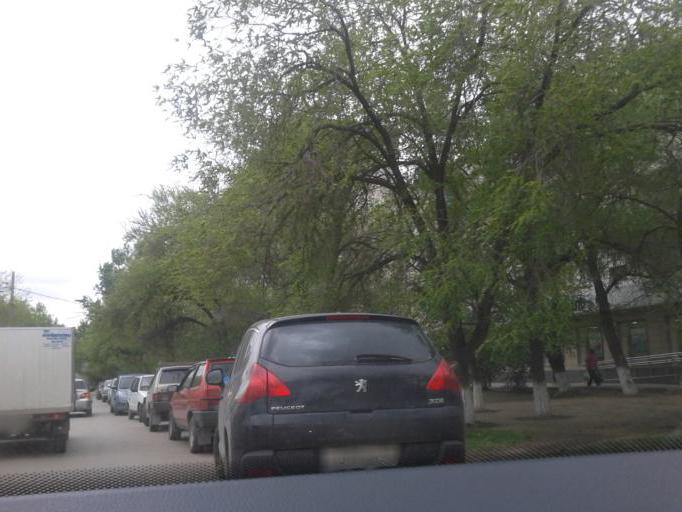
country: RU
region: Volgograd
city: Volgograd
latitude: 48.6080
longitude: 44.4216
